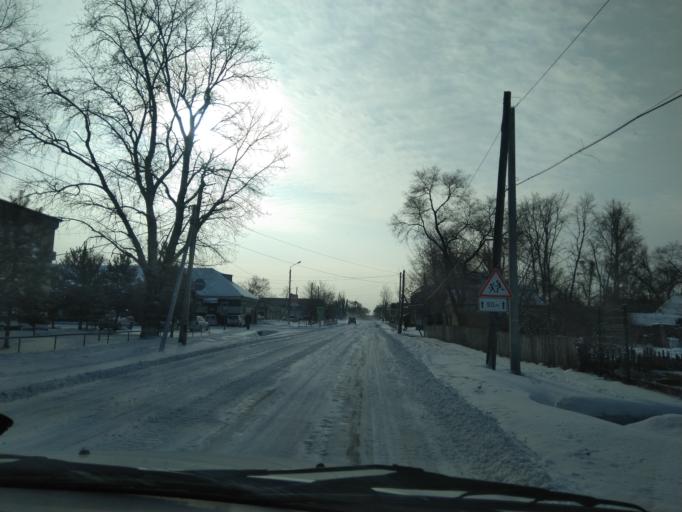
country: RU
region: Amur
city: Poyarkovo
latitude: 49.6237
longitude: 128.6508
